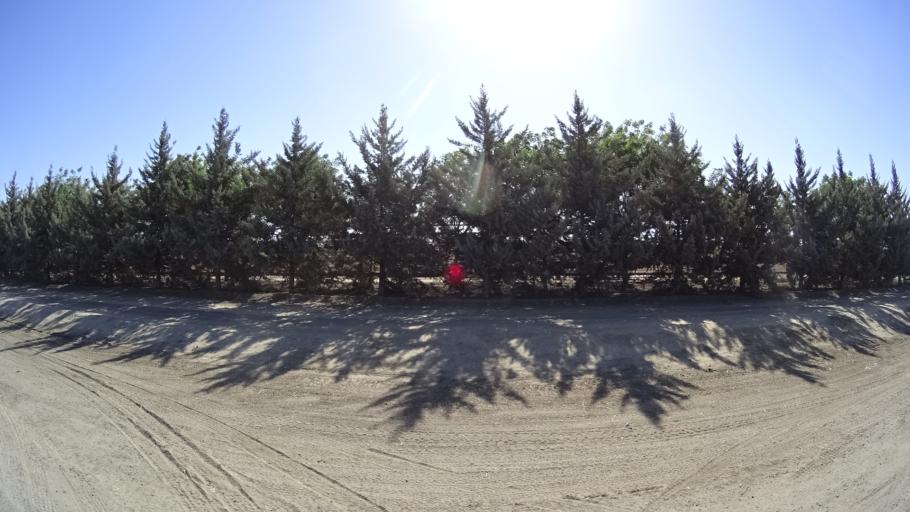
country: US
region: California
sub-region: Kings County
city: Corcoran
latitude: 36.1823
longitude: -119.5643
